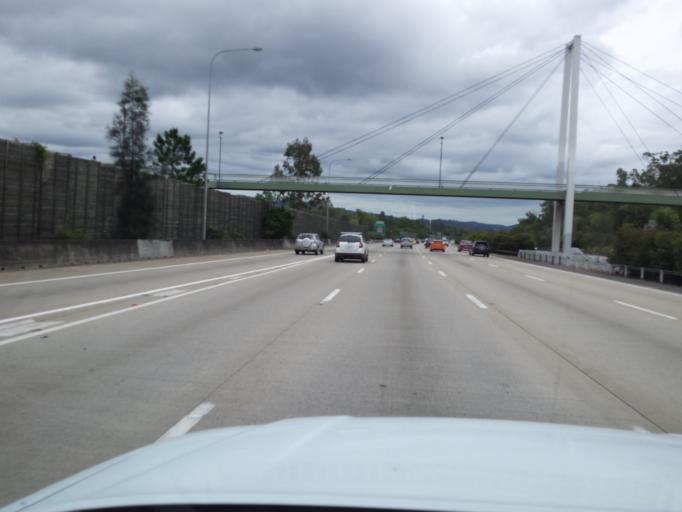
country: AU
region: Queensland
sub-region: Gold Coast
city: Upper Coomera
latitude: -27.9214
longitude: 153.3243
